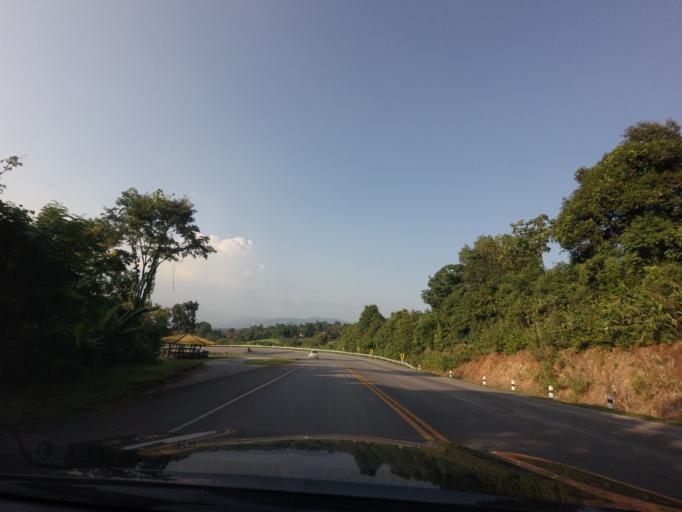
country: TH
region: Loei
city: Dan Sai
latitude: 17.2271
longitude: 101.1522
